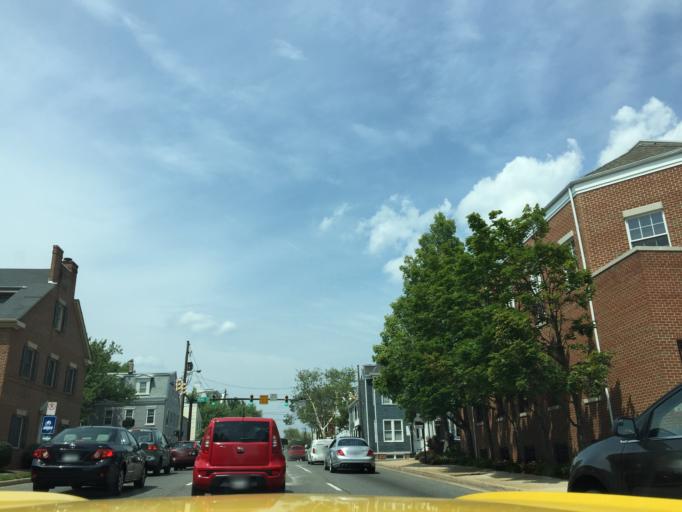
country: US
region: Virginia
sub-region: City of Alexandria
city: Alexandria
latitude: 38.8027
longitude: -77.0509
